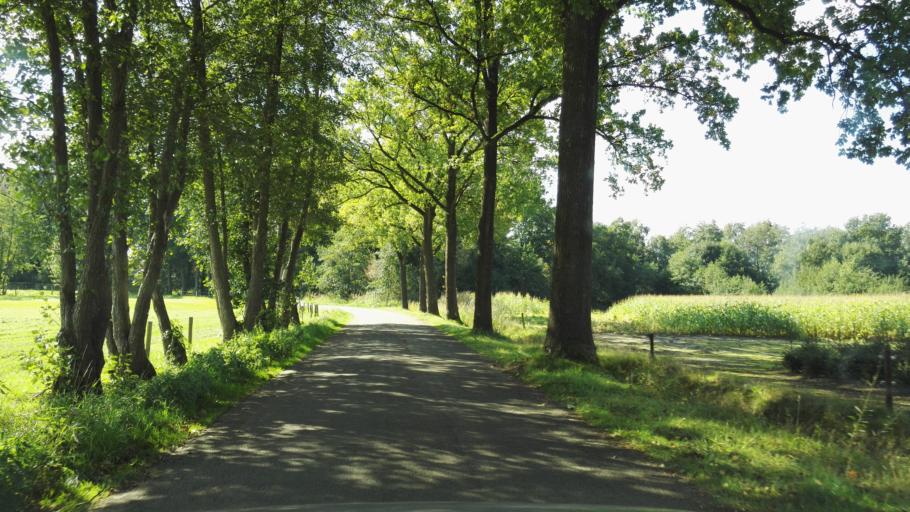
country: NL
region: Gelderland
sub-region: Gemeente Epe
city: Epe
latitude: 52.3343
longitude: 5.9886
